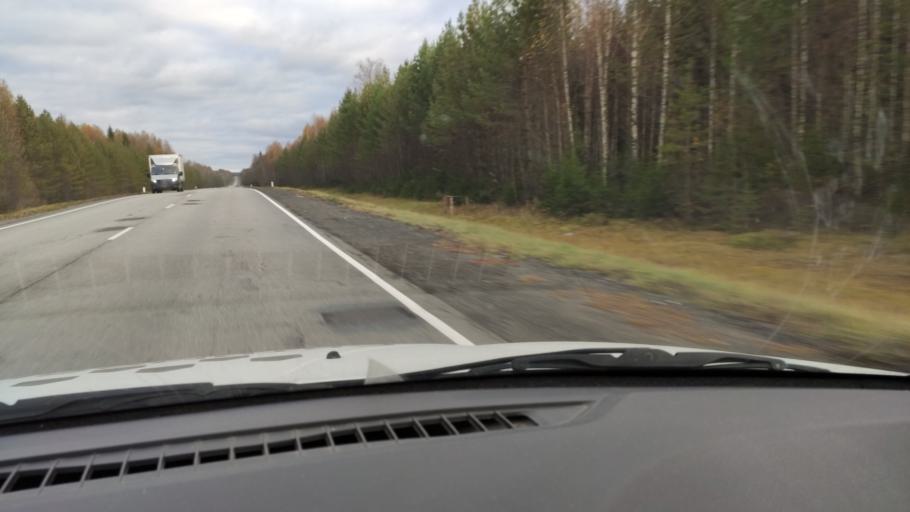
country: RU
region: Kirov
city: Dubrovka
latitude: 58.9044
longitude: 51.2730
